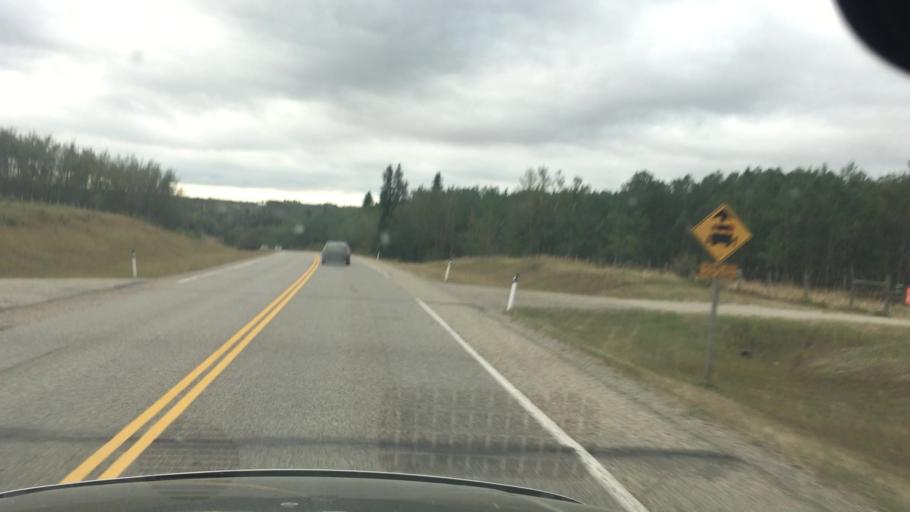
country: CA
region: Alberta
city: Cochrane
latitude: 51.3512
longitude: -114.4778
